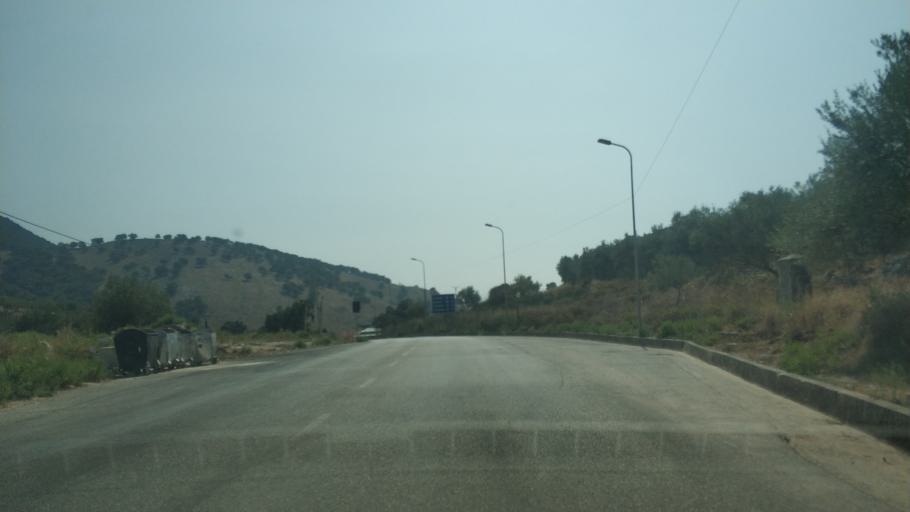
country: AL
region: Vlore
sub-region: Rrethi i Vlores
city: Himare
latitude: 40.0913
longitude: 19.7644
